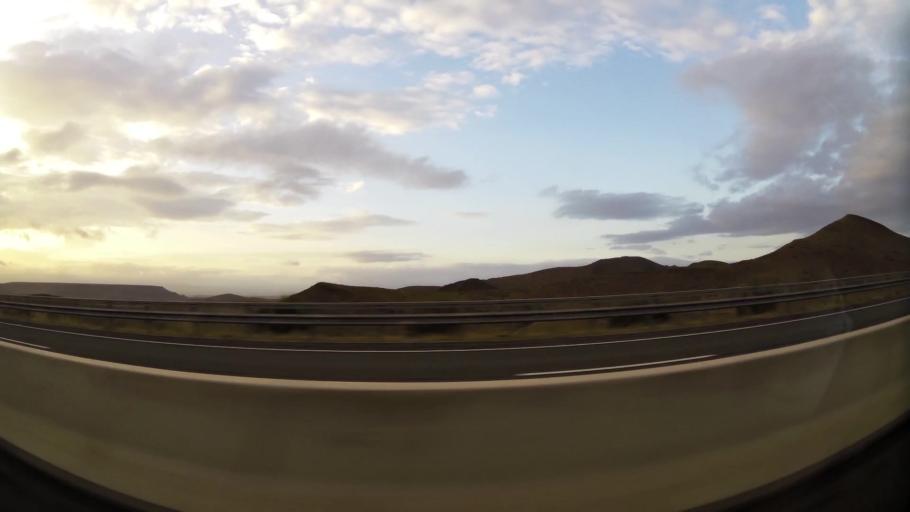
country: MA
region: Oriental
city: Taourirt
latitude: 34.4693
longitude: -3.0268
